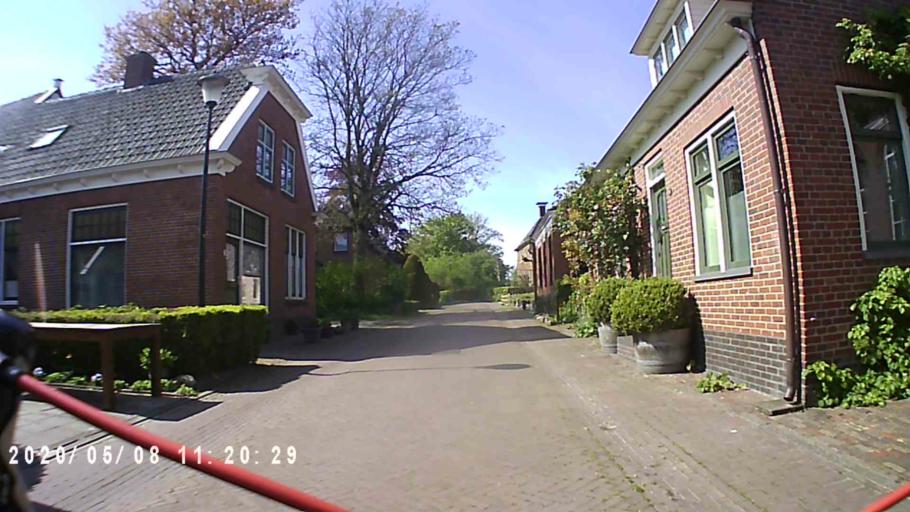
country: NL
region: Groningen
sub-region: Gemeente Bedum
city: Bedum
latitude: 53.3456
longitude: 6.6745
